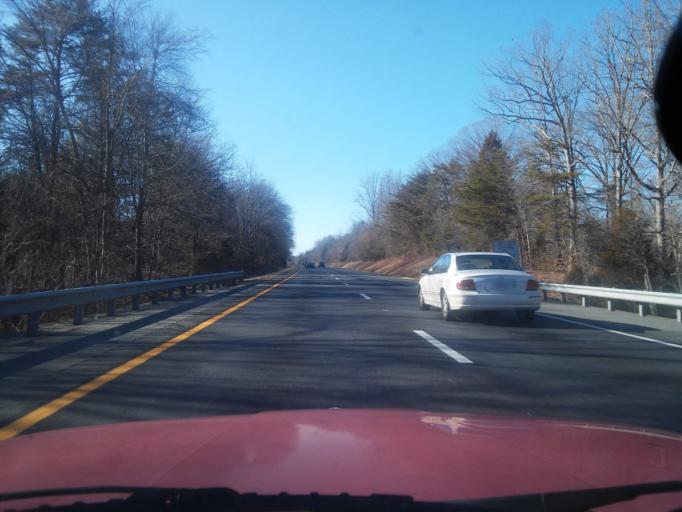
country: US
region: Virginia
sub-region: Fluvanna County
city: Lake Monticello
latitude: 38.0086
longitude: -78.3691
